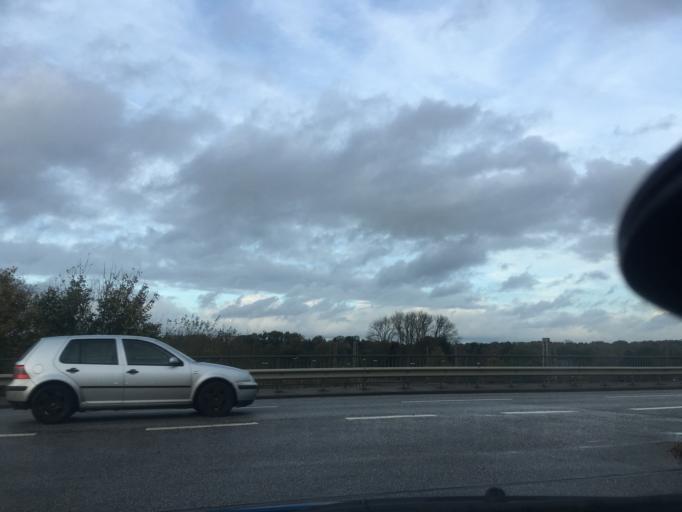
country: DE
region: Lower Saxony
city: Lueneburg
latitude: 53.2387
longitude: 10.4206
